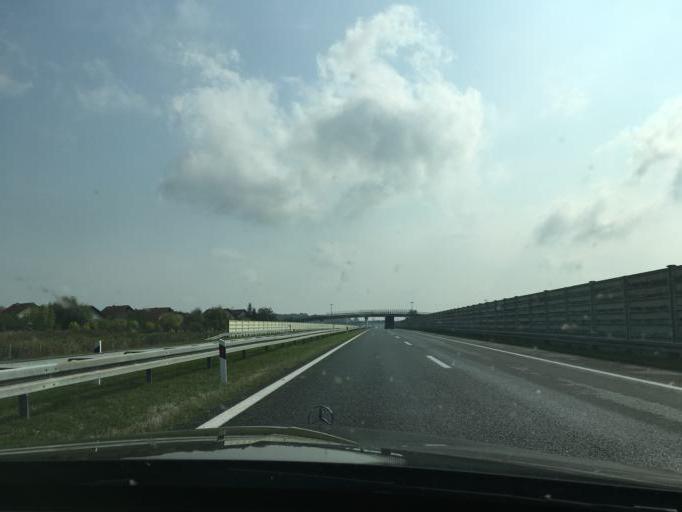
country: HR
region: Brodsko-Posavska
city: Bukovlje
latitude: 45.1804
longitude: 18.0559
